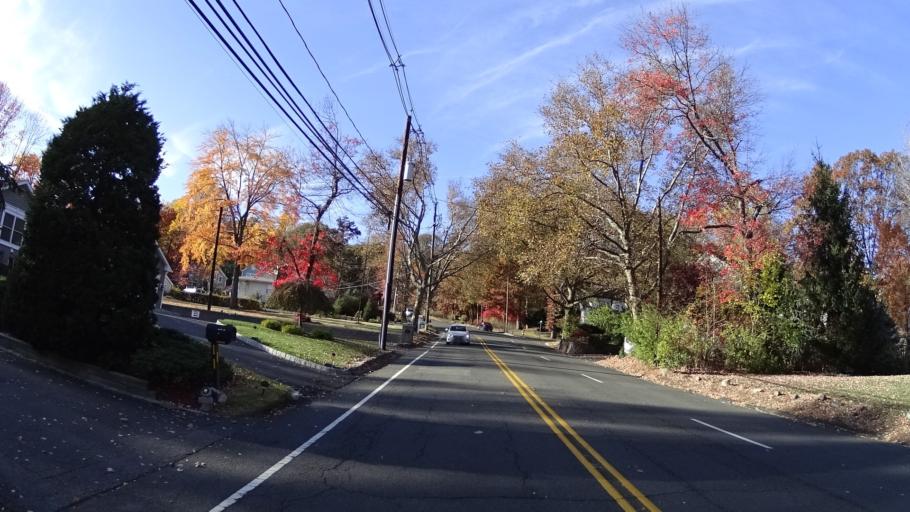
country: US
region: New Jersey
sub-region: Union County
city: Mountainside
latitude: 40.6870
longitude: -74.3496
